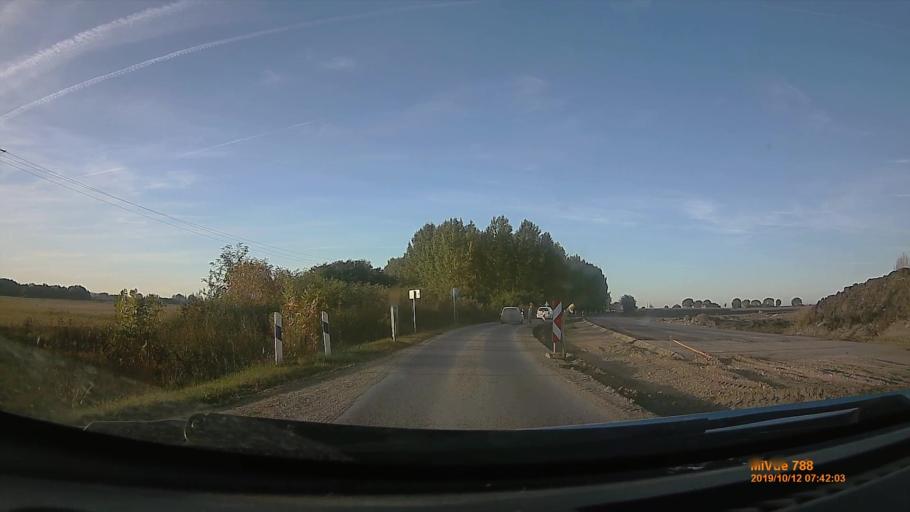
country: HU
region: Hajdu-Bihar
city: Pocsaj
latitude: 47.2037
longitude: 21.7953
